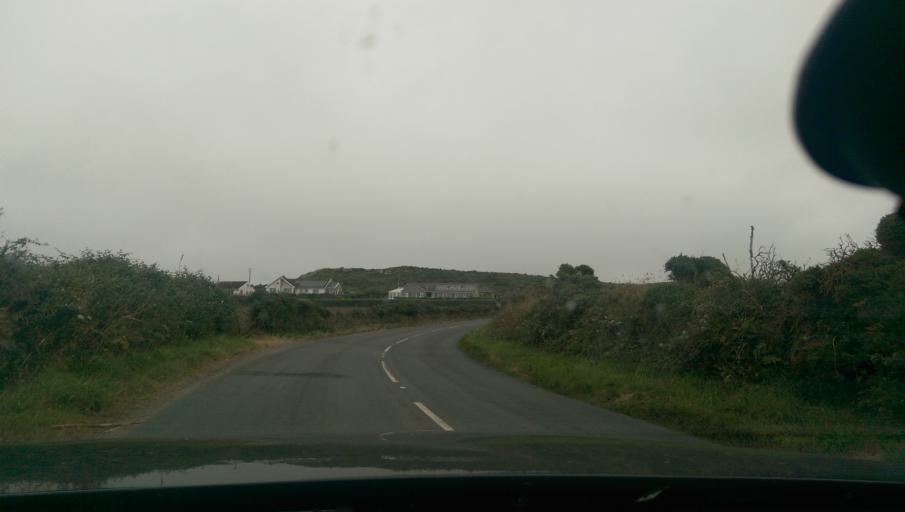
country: GB
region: England
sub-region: Cornwall
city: Saint Just
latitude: 50.1171
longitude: -5.6796
